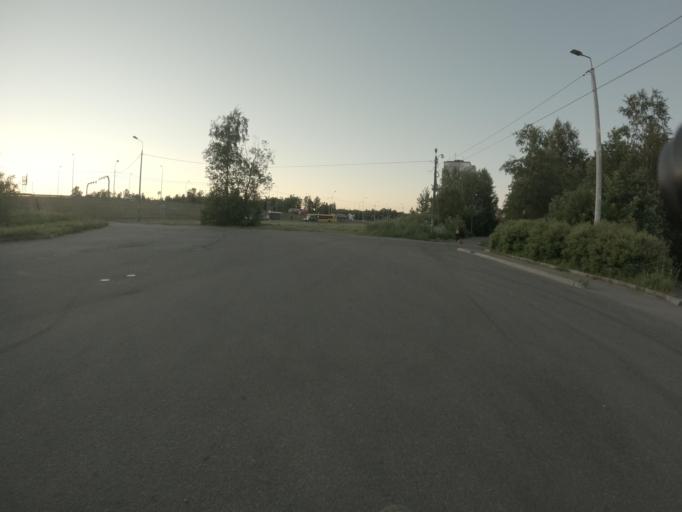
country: RU
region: St.-Petersburg
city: Krasnogvargeisky
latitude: 59.9838
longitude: 30.5169
